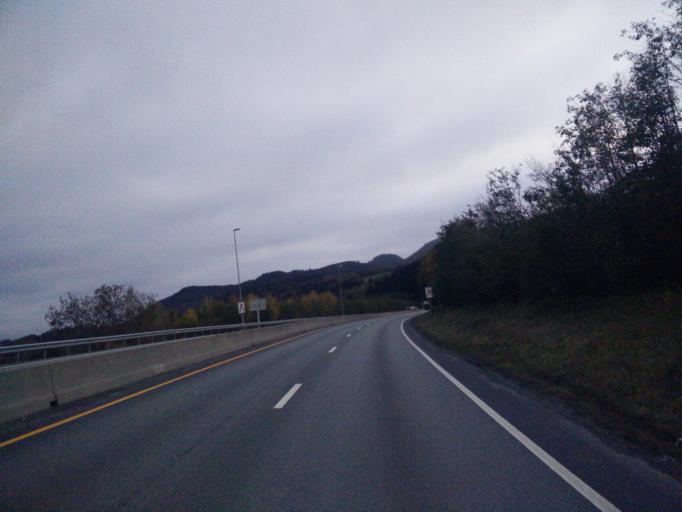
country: NO
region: Sor-Trondelag
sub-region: Malvik
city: Malvik
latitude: 63.4229
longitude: 10.5461
